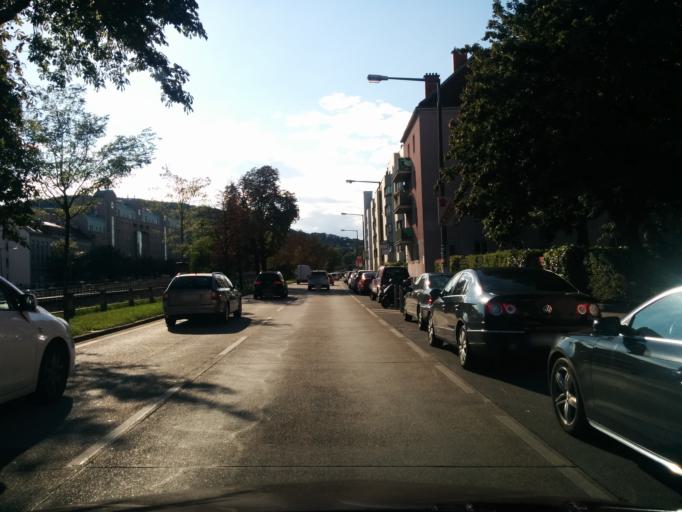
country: AT
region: Lower Austria
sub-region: Politischer Bezirk Modling
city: Perchtoldsdorf
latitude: 48.1931
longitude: 16.2715
